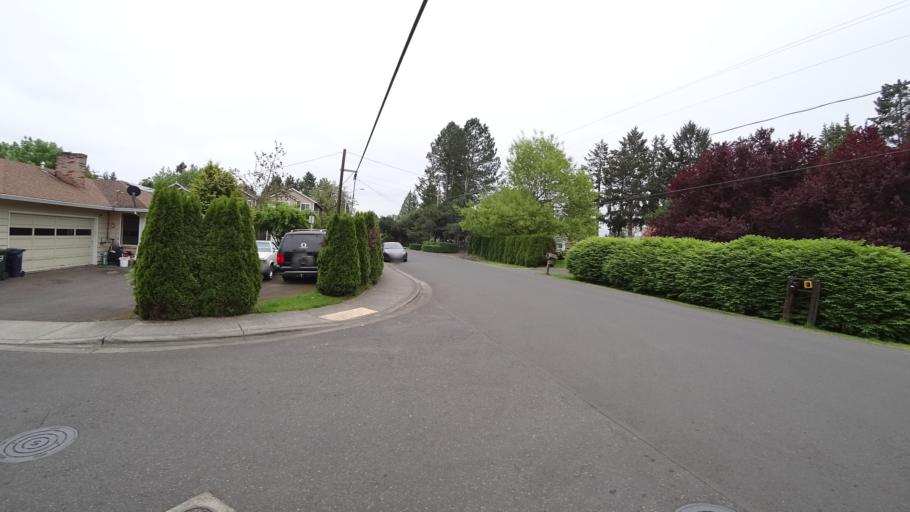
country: US
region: Oregon
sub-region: Washington County
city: Aloha
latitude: 45.5026
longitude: -122.8751
